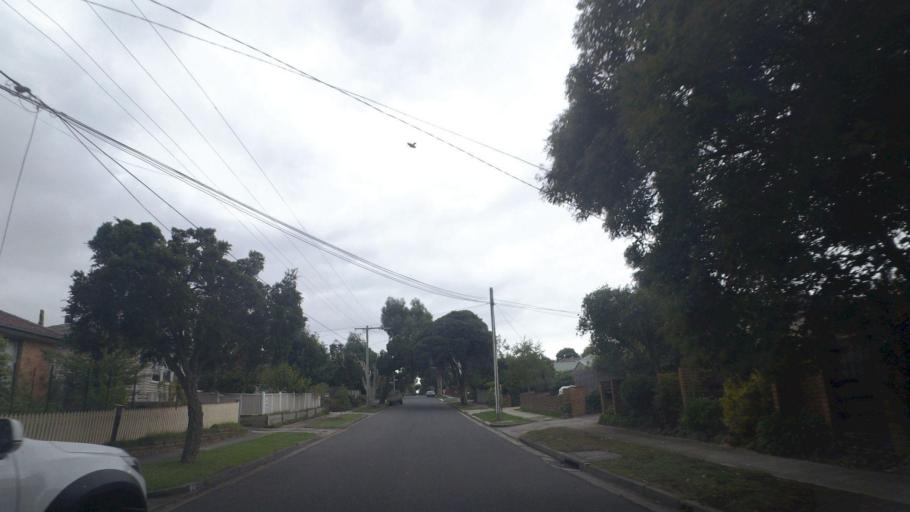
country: AU
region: Victoria
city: Forest Hill
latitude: -37.8347
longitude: 145.1760
